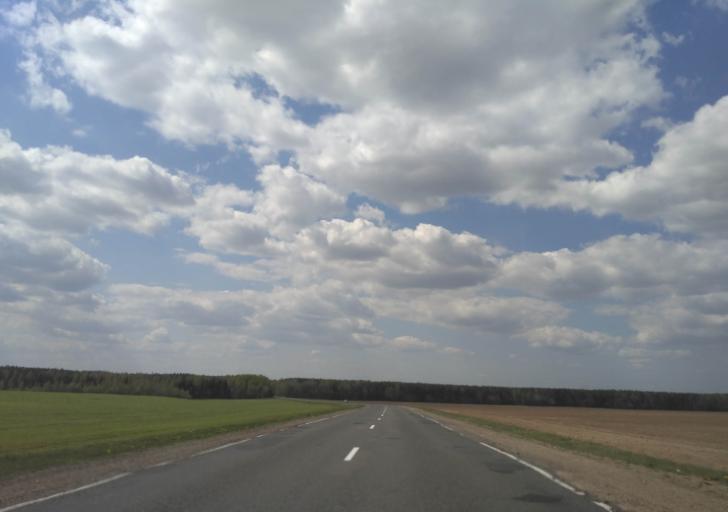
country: BY
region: Minsk
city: Vilyeyka
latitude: 54.5175
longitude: 27.0213
